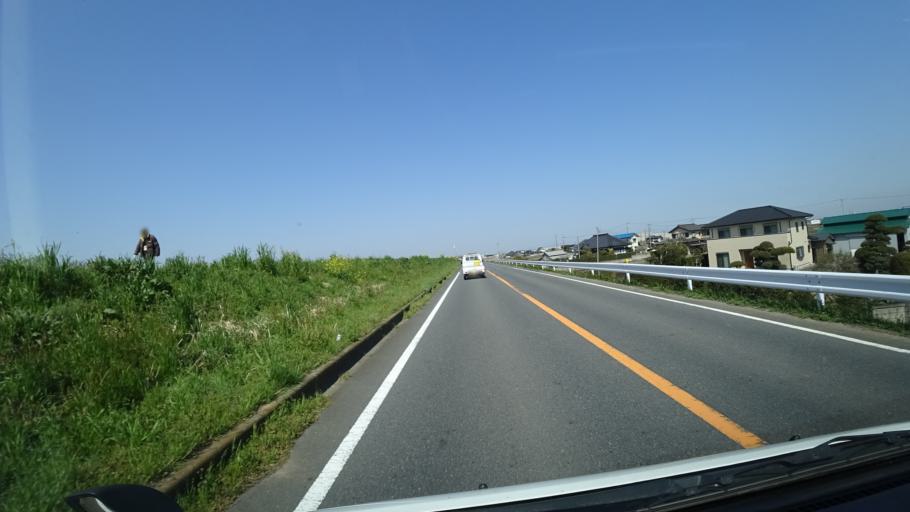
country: JP
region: Chiba
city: Katori-shi
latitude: 35.9153
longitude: 140.4792
